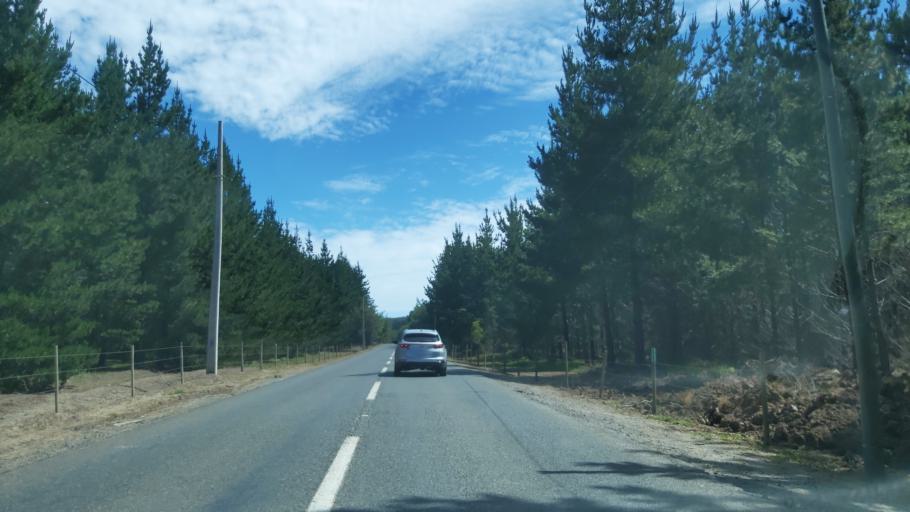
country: CL
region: Maule
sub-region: Provincia de Talca
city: Constitucion
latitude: -35.5305
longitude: -72.5418
